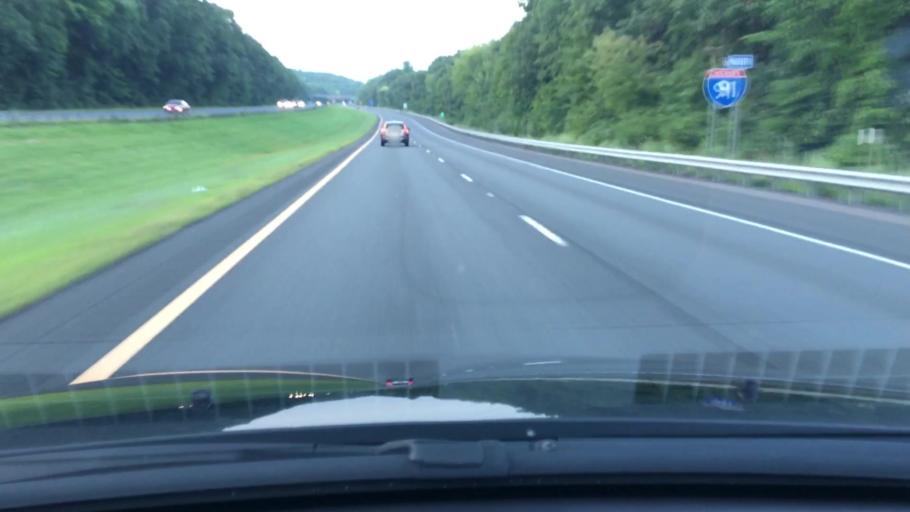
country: US
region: Massachusetts
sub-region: Hampden County
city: Holyoke
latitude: 42.2334
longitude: -72.6338
